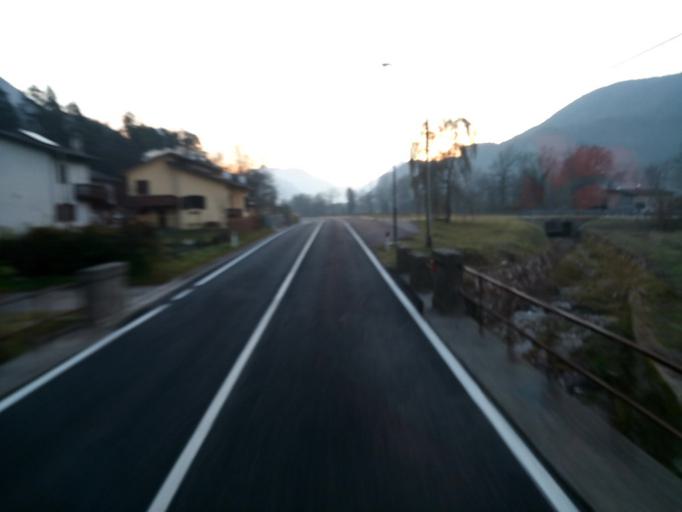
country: IT
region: Friuli Venezia Giulia
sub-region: Provincia di Udine
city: Villa Santina
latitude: 46.4128
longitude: 12.9361
